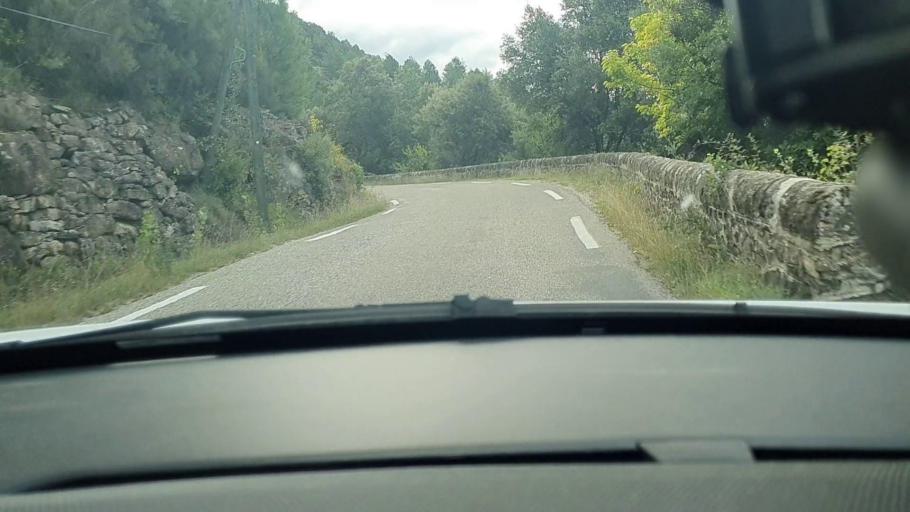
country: FR
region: Languedoc-Roussillon
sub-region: Departement du Gard
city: Besseges
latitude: 44.3484
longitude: 4.0228
